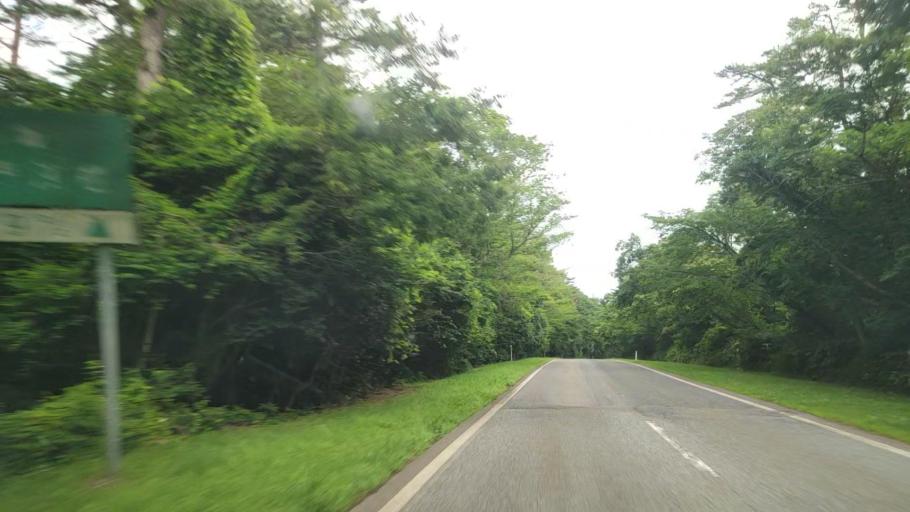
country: JP
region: Tottori
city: Yonago
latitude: 35.4032
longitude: 133.4856
